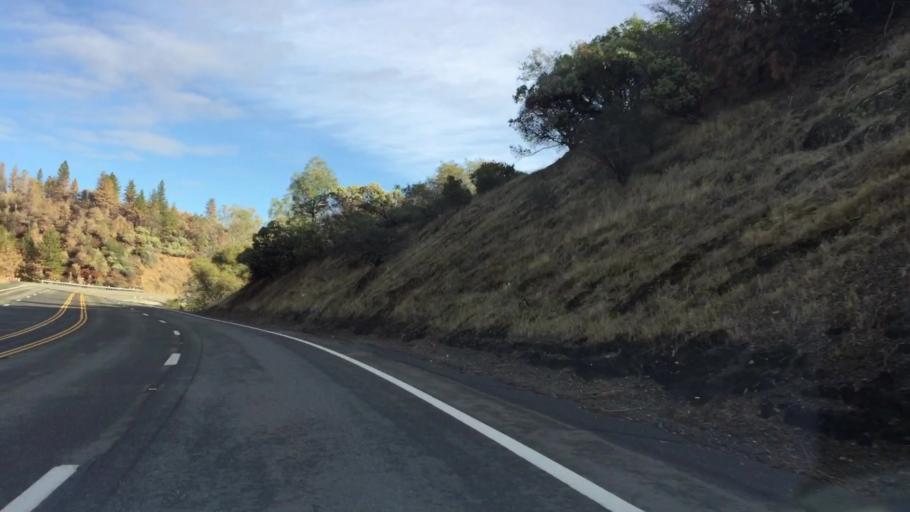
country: US
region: California
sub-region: Butte County
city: Paradise
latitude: 39.6898
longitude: -121.5348
